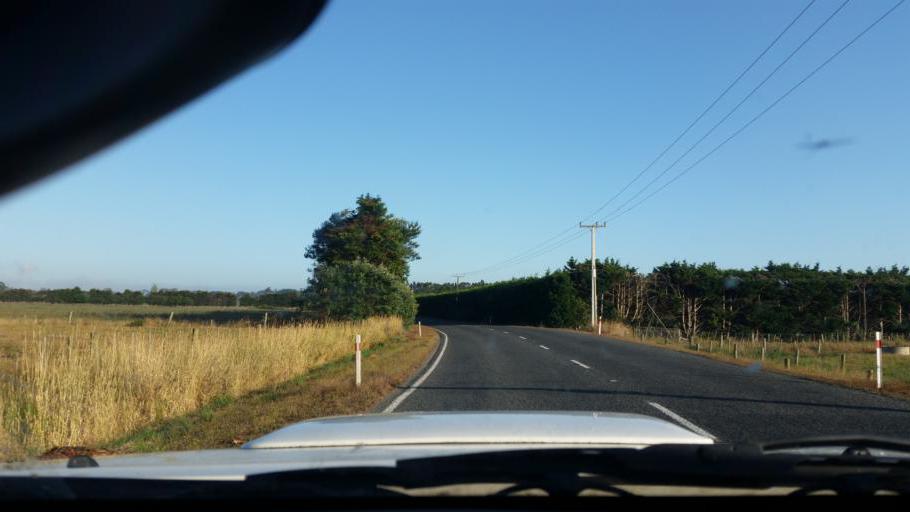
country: NZ
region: Northland
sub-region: Kaipara District
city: Dargaville
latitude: -35.9886
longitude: 173.8837
